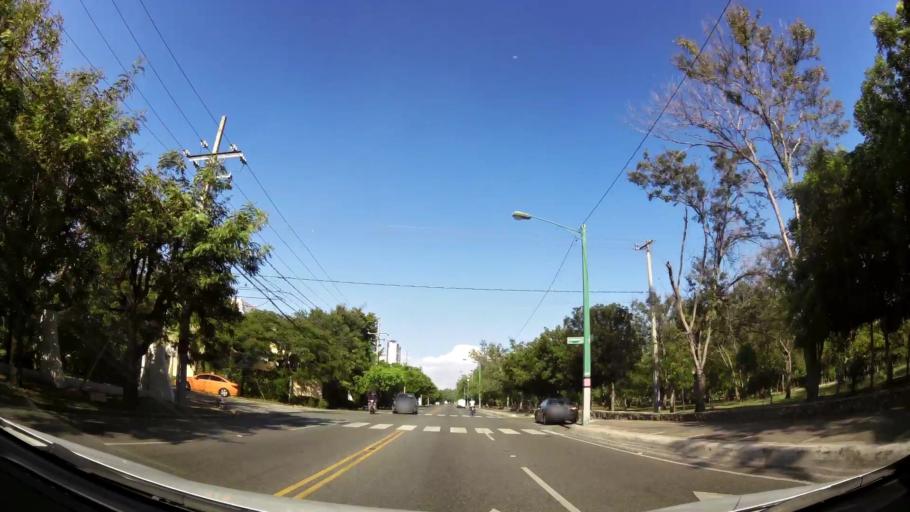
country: DO
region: Nacional
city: Bella Vista
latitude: 18.4437
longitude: -69.9552
